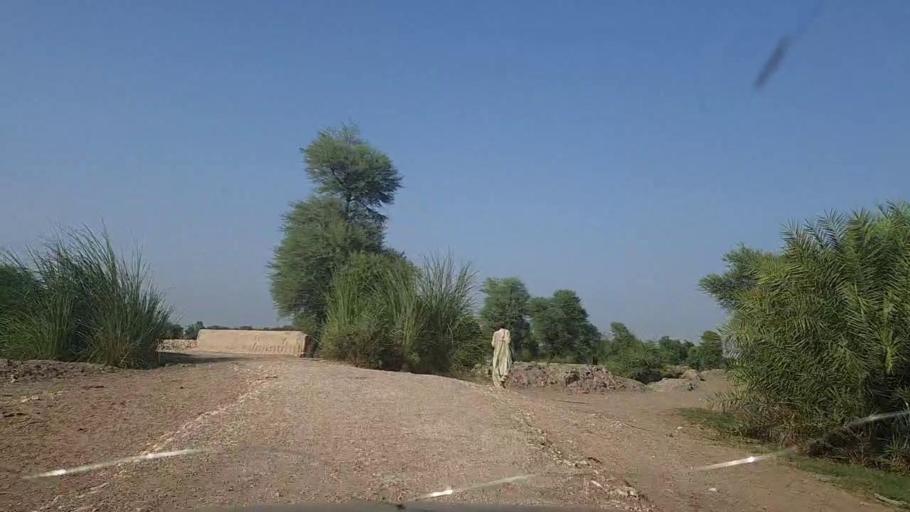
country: PK
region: Sindh
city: Khanpur
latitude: 27.7082
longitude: 69.3318
